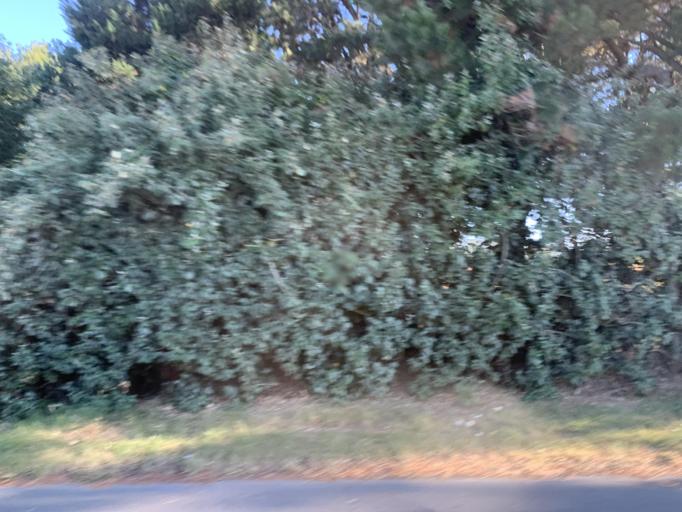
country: FR
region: Pays de la Loire
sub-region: Departement de la Loire-Atlantique
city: Pornichet
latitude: 47.2587
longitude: -2.2758
